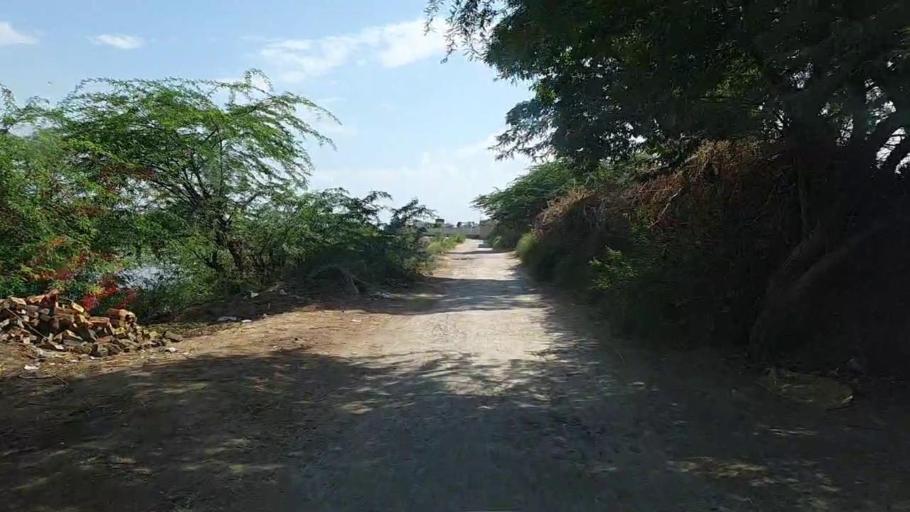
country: PK
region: Sindh
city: Bhiria
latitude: 26.9018
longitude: 68.2268
